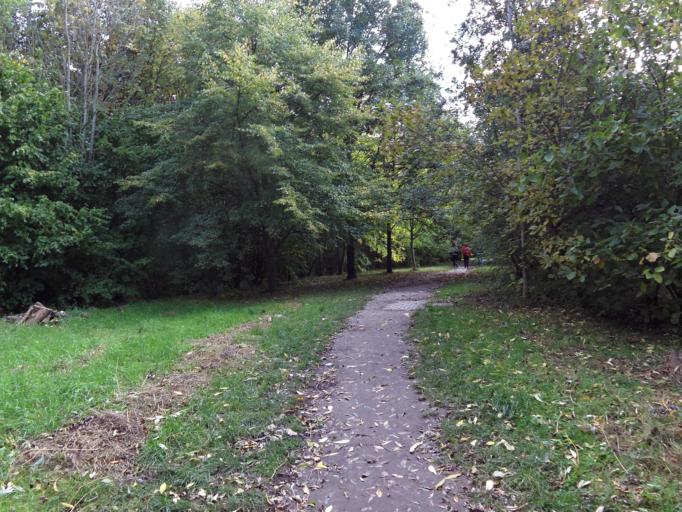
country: DE
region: Saxony
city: Grossposna
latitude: 51.3076
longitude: 12.4467
